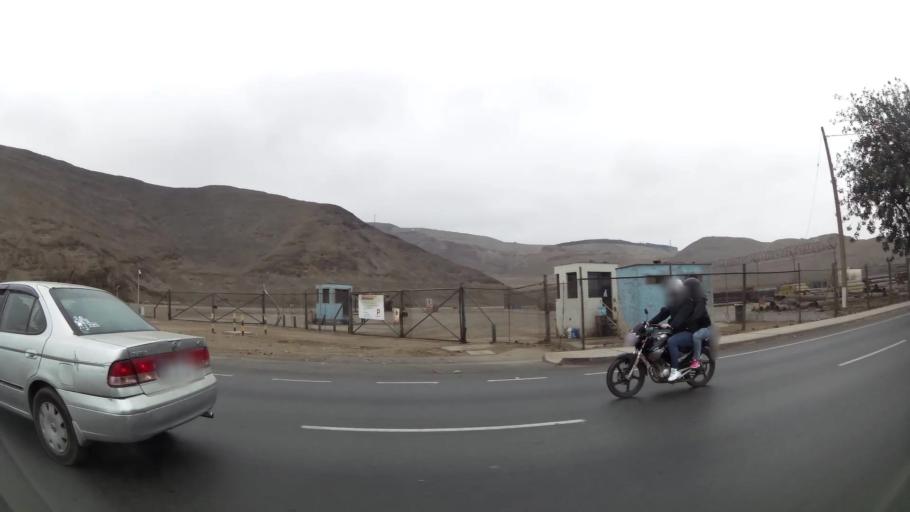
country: PE
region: Lima
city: Ventanilla
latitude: -11.9292
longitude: -77.1301
